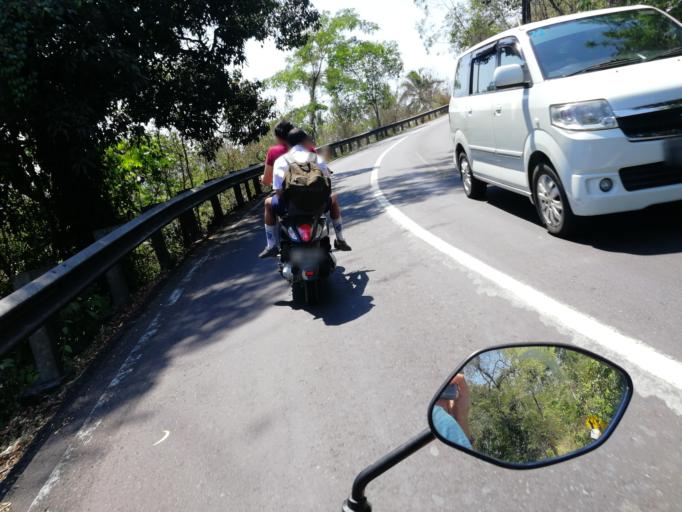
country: ID
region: Bali
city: Abang
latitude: -8.3916
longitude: 115.5973
